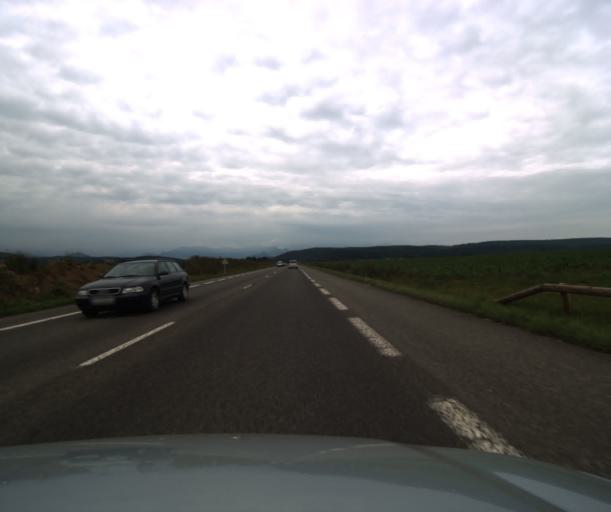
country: FR
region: Midi-Pyrenees
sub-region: Departement des Hautes-Pyrenees
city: Ossun
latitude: 43.1694
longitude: -0.0043
